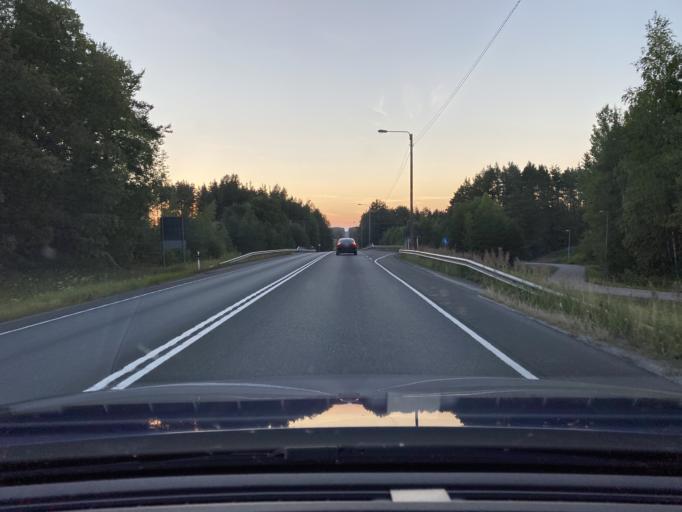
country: FI
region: Pirkanmaa
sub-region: Luoteis-Pirkanmaa
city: Ikaalinen
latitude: 61.7635
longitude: 23.0220
